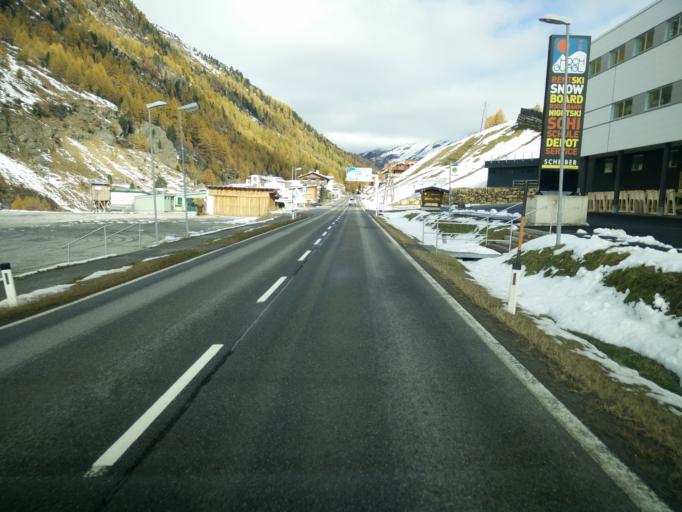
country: AT
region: Tyrol
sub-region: Politischer Bezirk Imst
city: Soelden
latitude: 46.8977
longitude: 11.0402
